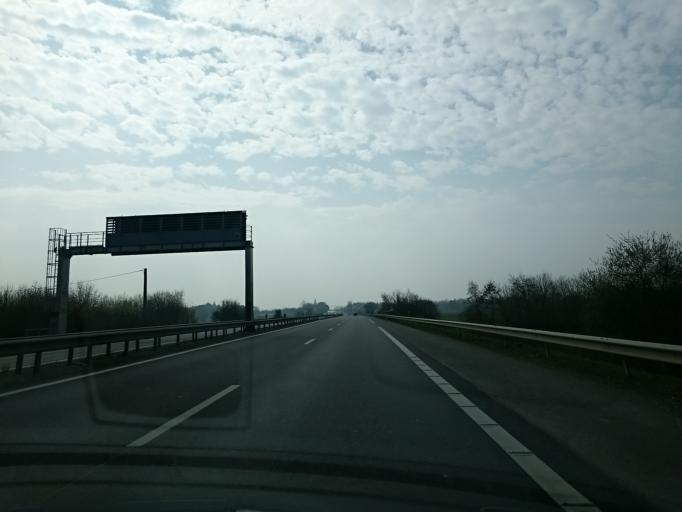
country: FR
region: Brittany
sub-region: Departement d'Ille-et-Vilaine
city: Chartres-de-Bretagne
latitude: 48.0273
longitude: -1.6900
